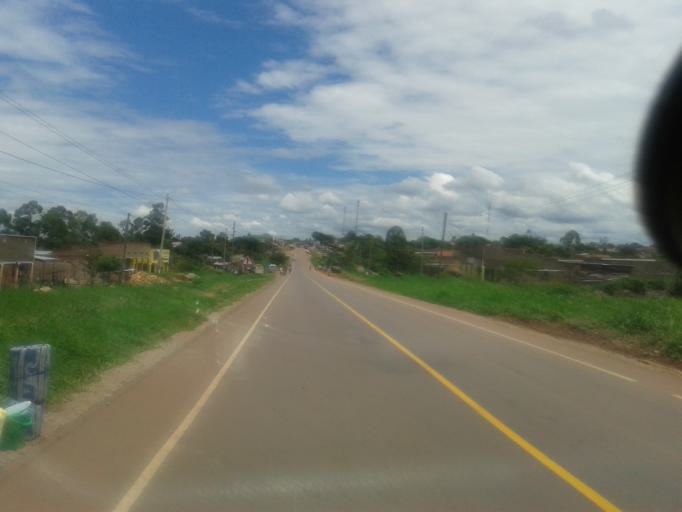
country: UG
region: Western Region
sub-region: Kiryandongo District
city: Kiryandongo
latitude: 1.8136
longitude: 32.0138
